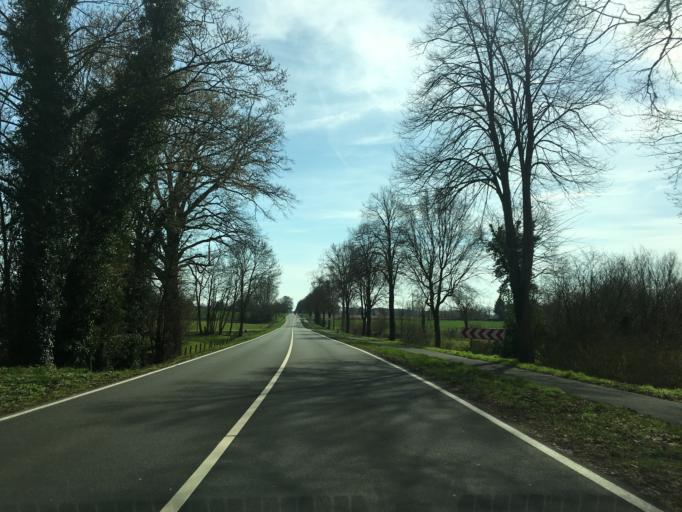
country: DE
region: North Rhine-Westphalia
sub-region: Regierungsbezirk Munster
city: Greven
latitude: 52.0715
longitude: 7.6128
